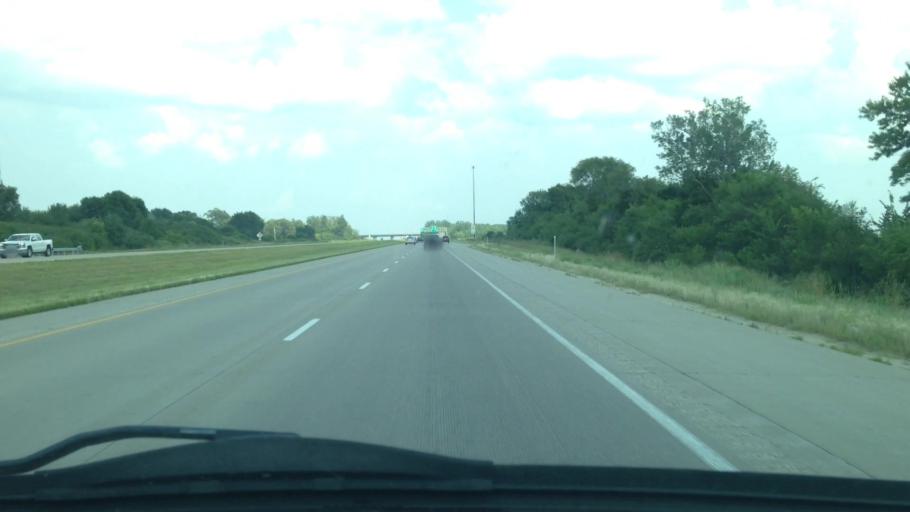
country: US
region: Iowa
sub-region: Black Hawk County
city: Elk Run Heights
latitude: 42.4492
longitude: -92.2082
